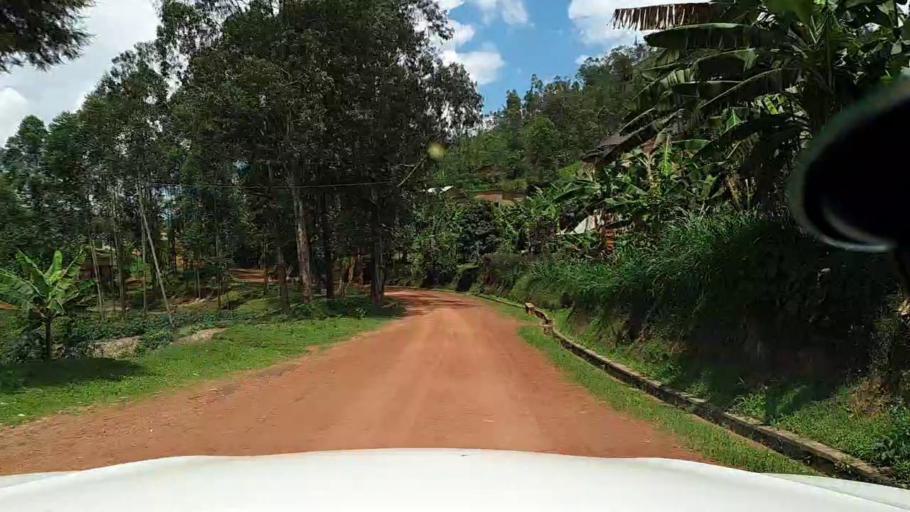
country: RW
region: Northern Province
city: Byumba
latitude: -1.6975
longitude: 29.8305
